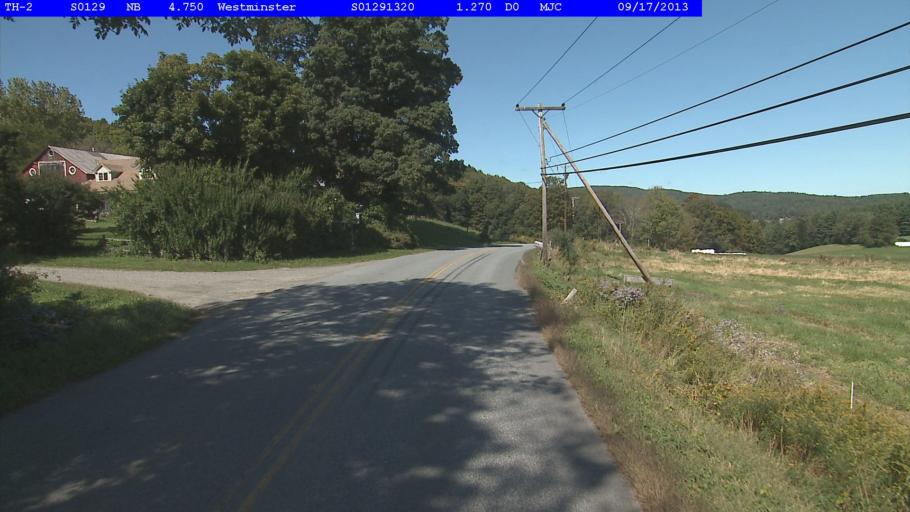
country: US
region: New Hampshire
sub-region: Cheshire County
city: Westmoreland
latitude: 43.0390
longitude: -72.5264
